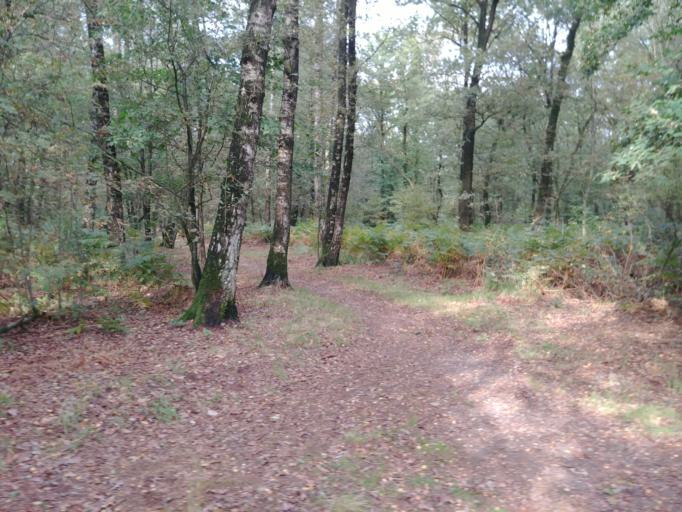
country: NL
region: Gelderland
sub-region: Gemeente Renkum
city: Doorwerth
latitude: 51.9823
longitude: 5.7898
